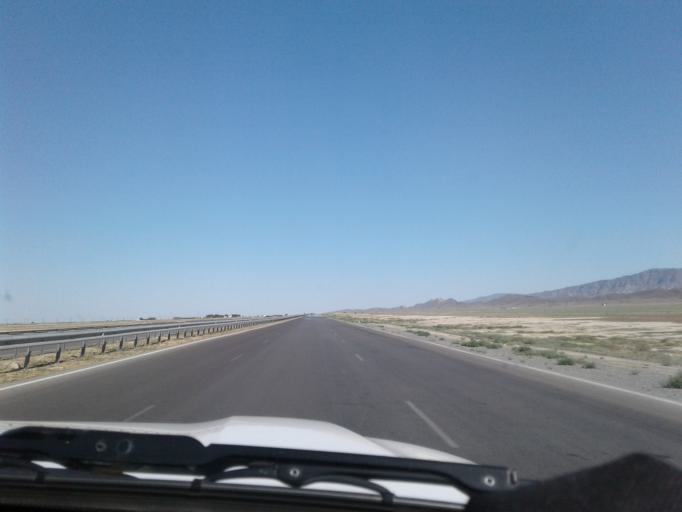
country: IR
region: Razavi Khorasan
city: Dargaz
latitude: 37.7362
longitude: 58.9849
